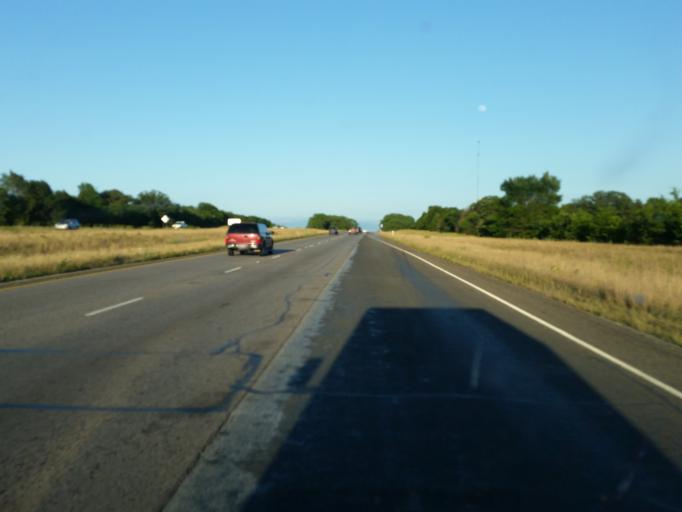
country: US
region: Texas
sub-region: Van Zandt County
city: Wills Point
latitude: 32.6673
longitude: -96.1418
